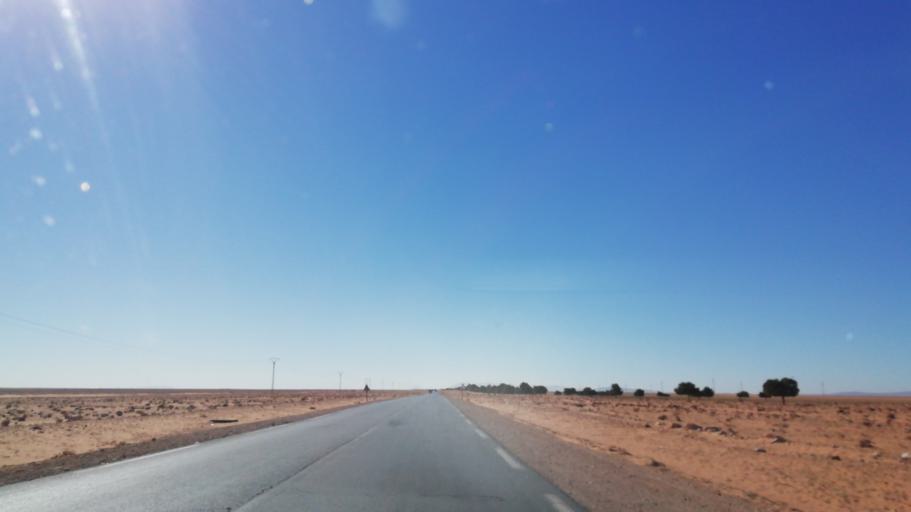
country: DZ
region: Wilaya de Naama
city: Naama
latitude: 33.9777
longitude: 0.0261
